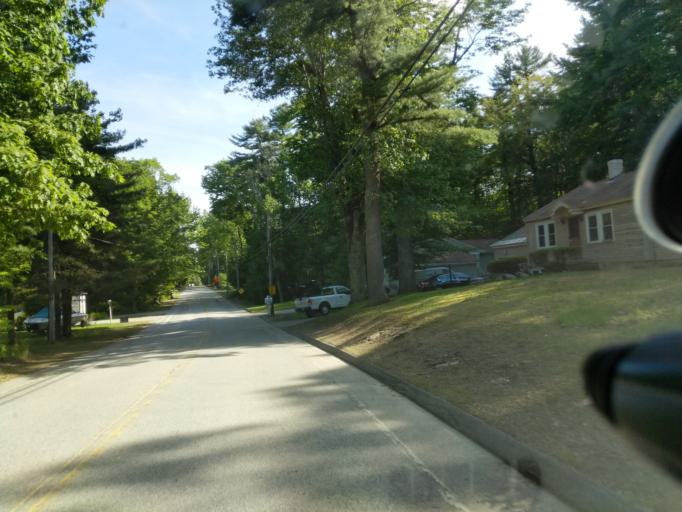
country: US
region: Maine
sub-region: Cumberland County
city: Falmouth
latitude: 43.7362
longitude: -70.3058
